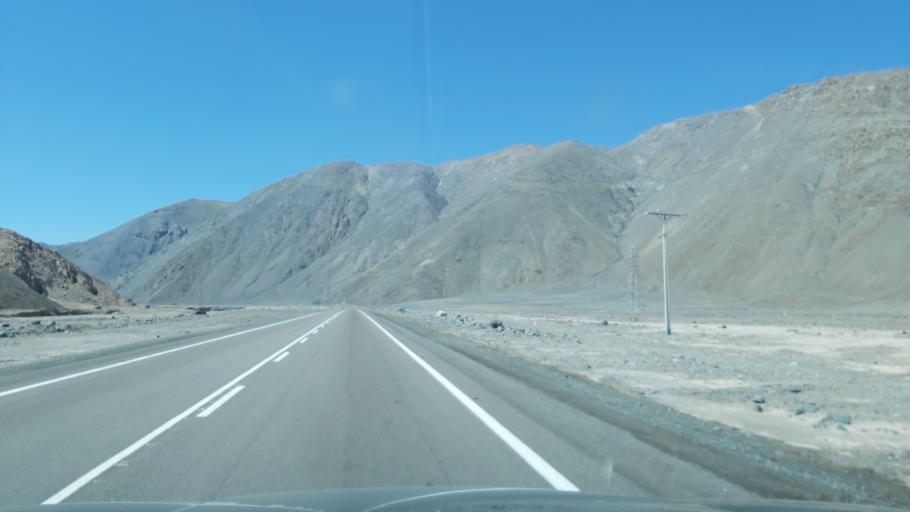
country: CL
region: Atacama
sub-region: Provincia de Chanaral
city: Diego de Almagro
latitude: -26.3416
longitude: -69.7452
